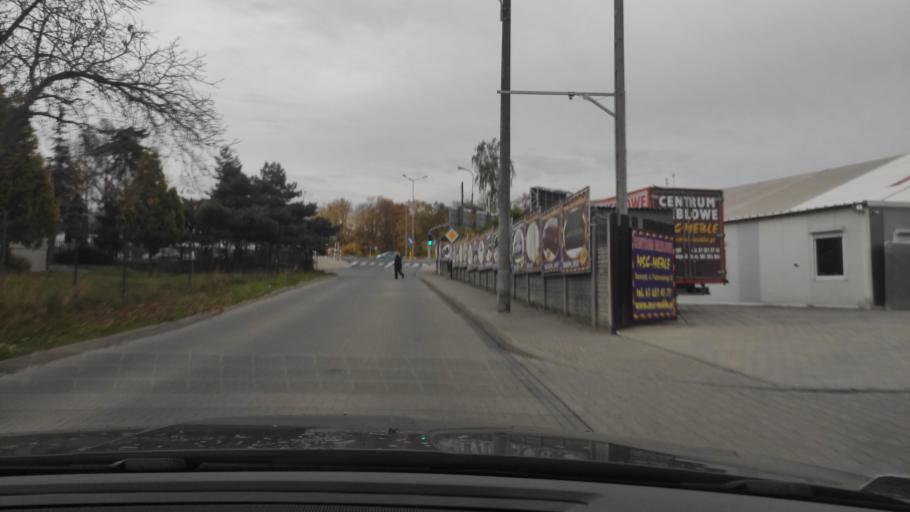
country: PL
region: Greater Poland Voivodeship
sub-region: Powiat poznanski
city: Swarzedz
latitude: 52.4061
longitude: 17.0613
